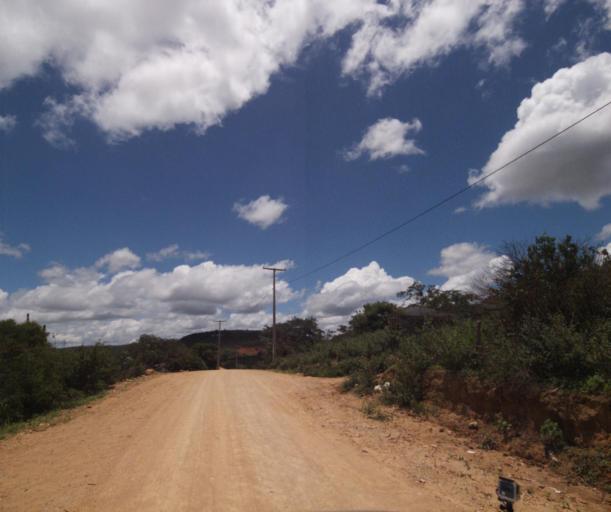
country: BR
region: Bahia
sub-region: Pocoes
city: Pocoes
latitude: -14.3856
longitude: -40.4197
